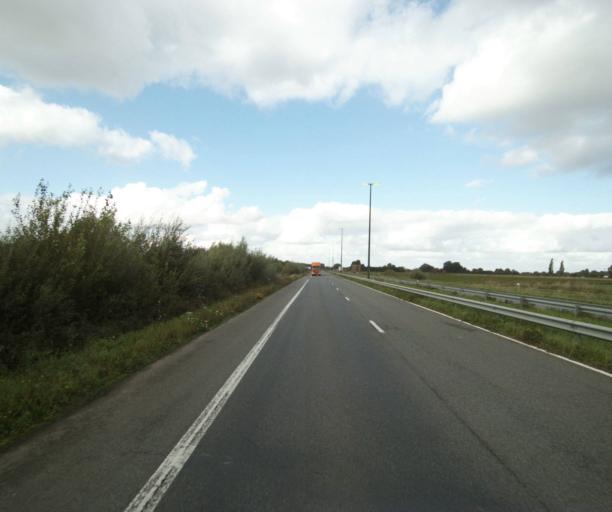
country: FR
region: Nord-Pas-de-Calais
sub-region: Departement du Nord
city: Frelinghien
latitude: 50.7172
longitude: 2.9137
